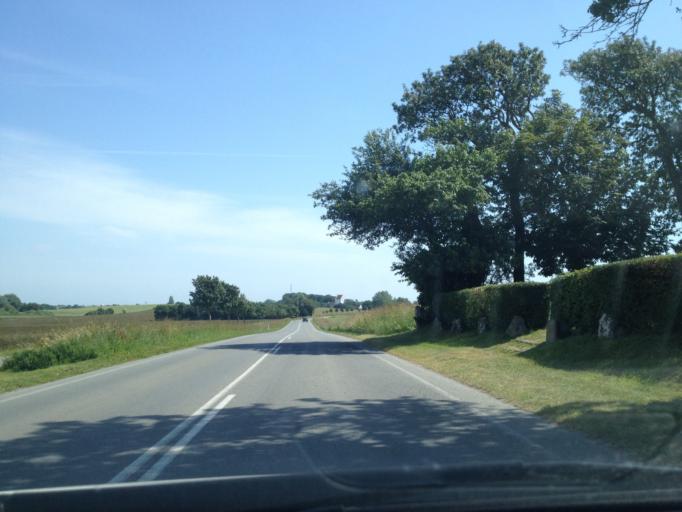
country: DK
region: Central Jutland
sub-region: Samso Kommune
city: Tranebjerg
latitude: 55.8405
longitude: 10.5767
